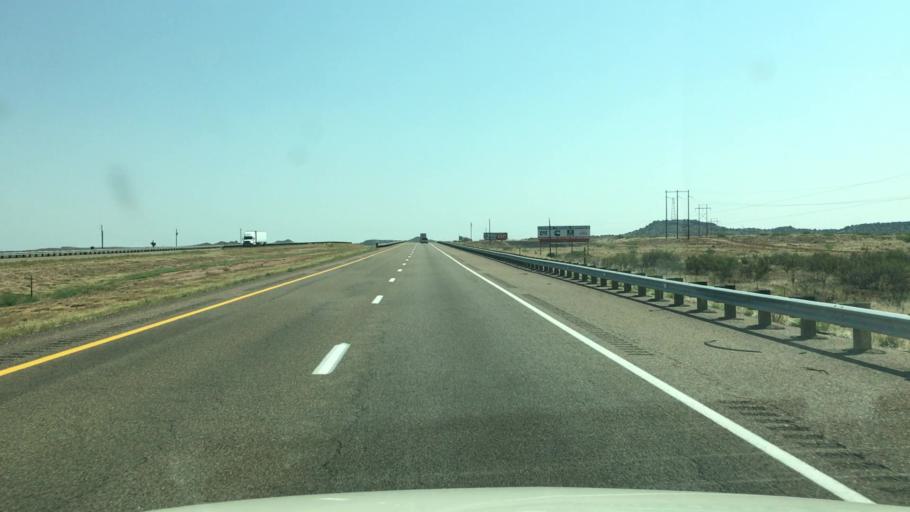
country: US
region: New Mexico
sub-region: Quay County
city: Tucumcari
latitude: 35.1206
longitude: -103.9709
